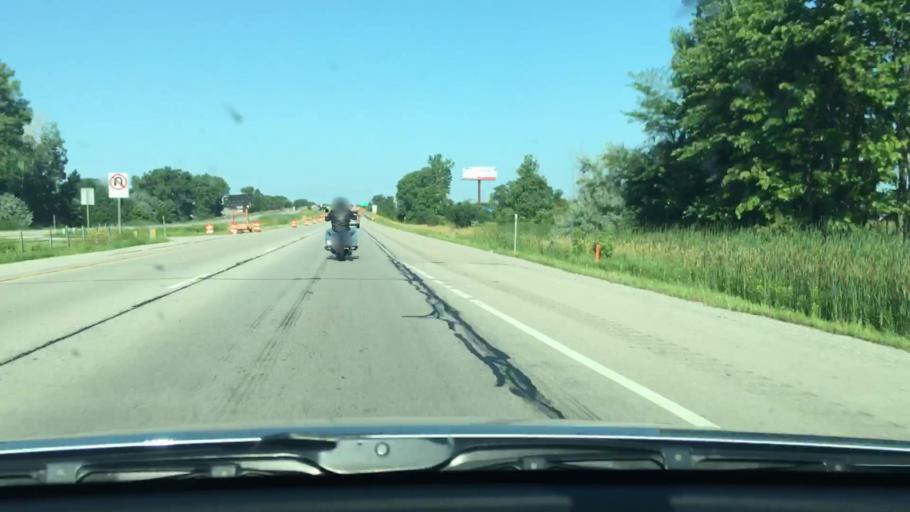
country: US
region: Wisconsin
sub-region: Outagamie County
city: Appleton
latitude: 44.2989
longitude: -88.4253
